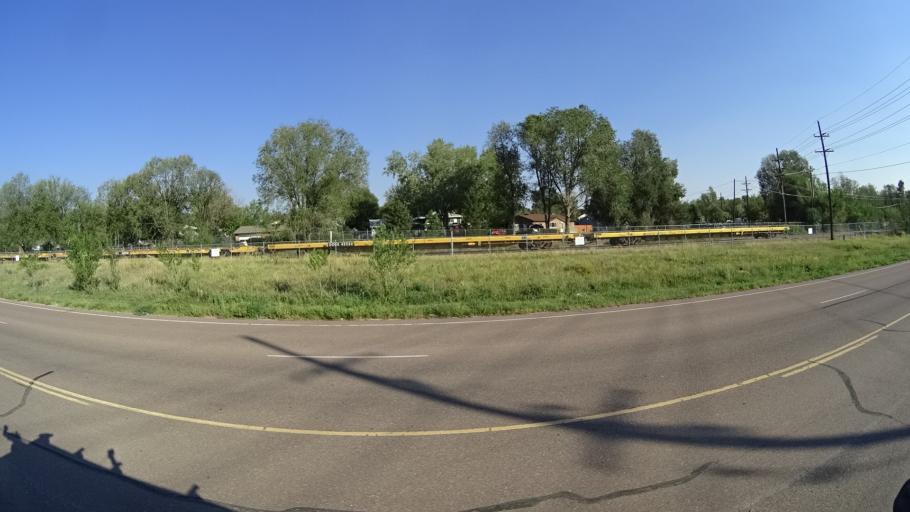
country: US
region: Colorado
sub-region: El Paso County
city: Stratmoor
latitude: 38.7733
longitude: -104.7947
